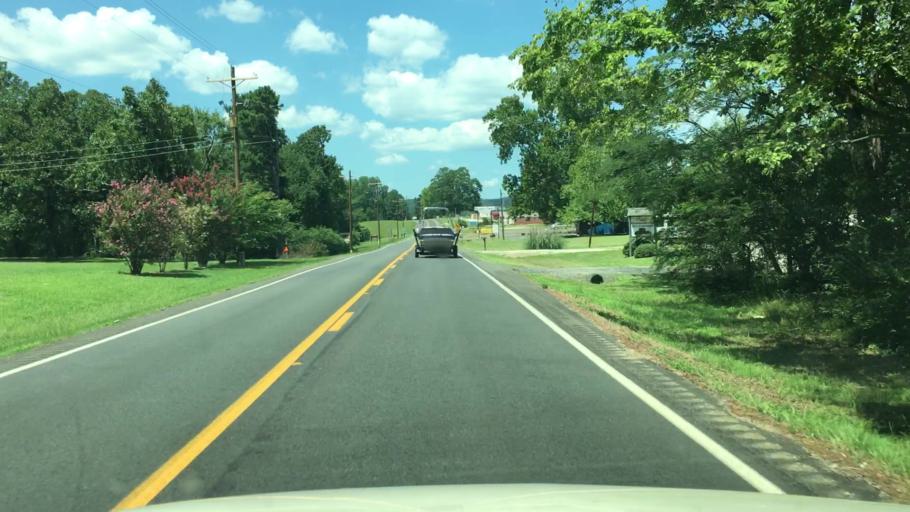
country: US
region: Arkansas
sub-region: Garland County
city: Lake Hamilton
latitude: 34.3215
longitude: -93.1729
